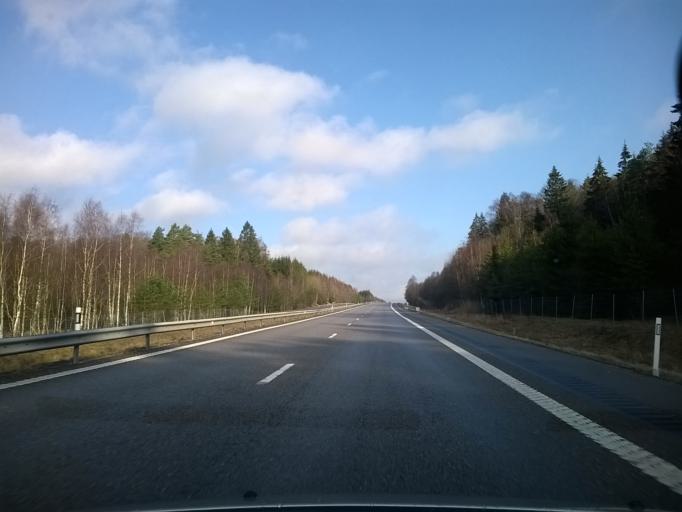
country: SE
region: Vaestra Goetaland
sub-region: Stenungsunds Kommun
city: Stenungsund
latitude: 58.0768
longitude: 11.8885
